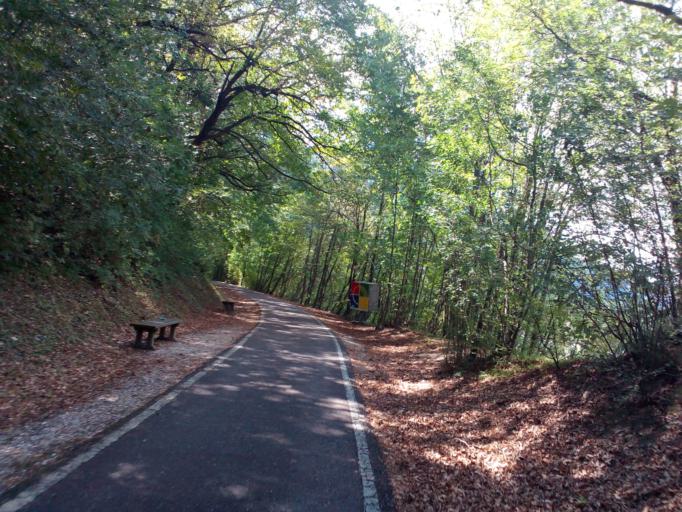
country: IT
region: Trentino-Alto Adige
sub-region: Bolzano
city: Cornaiano
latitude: 46.4765
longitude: 11.2839
